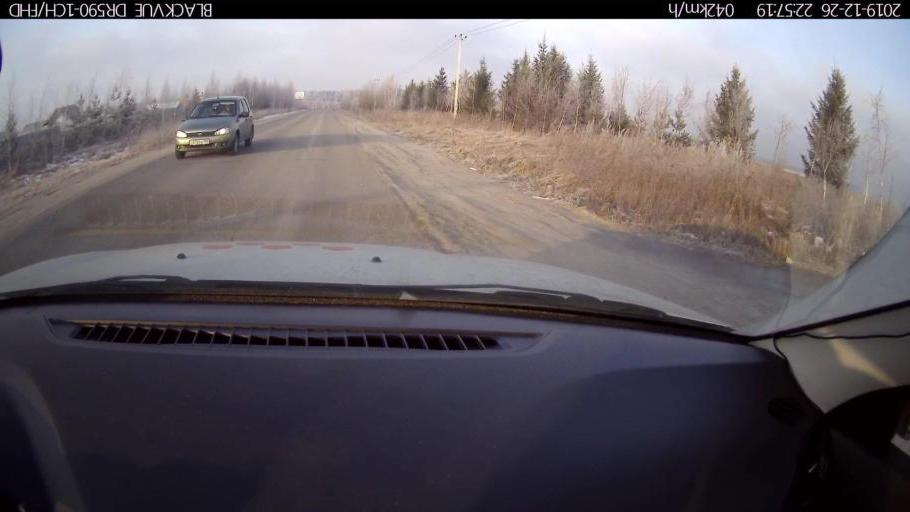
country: RU
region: Nizjnij Novgorod
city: Burevestnik
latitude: 56.1500
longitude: 43.7168
